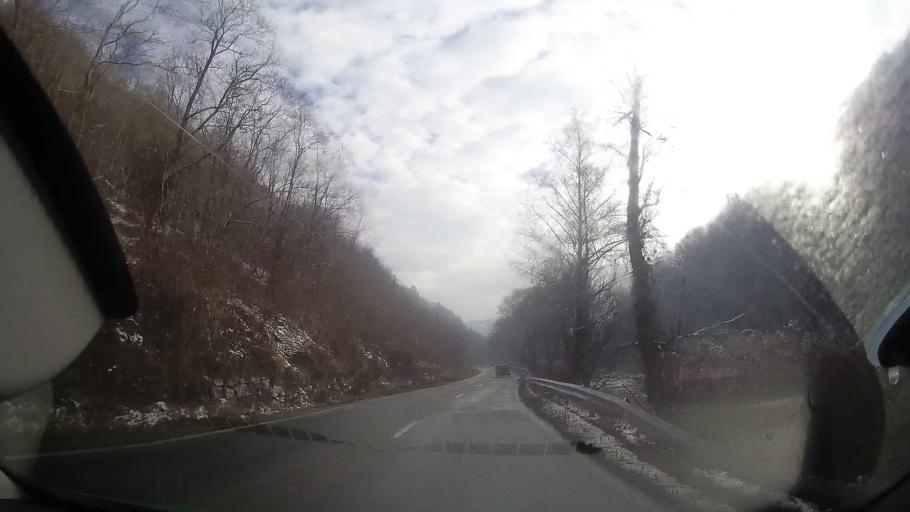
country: RO
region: Alba
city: Salciua de Sus
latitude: 46.3997
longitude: 23.3792
